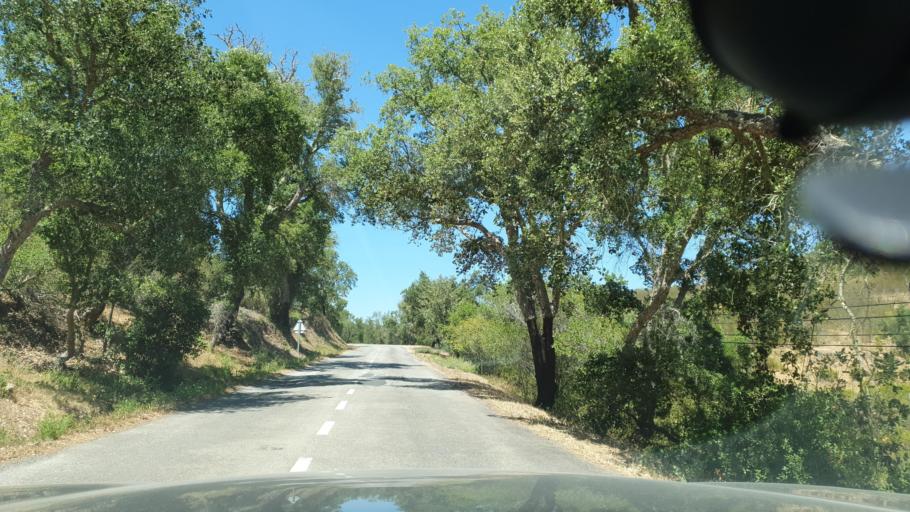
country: PT
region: Beja
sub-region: Odemira
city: Odemira
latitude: 37.6018
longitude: -8.4941
